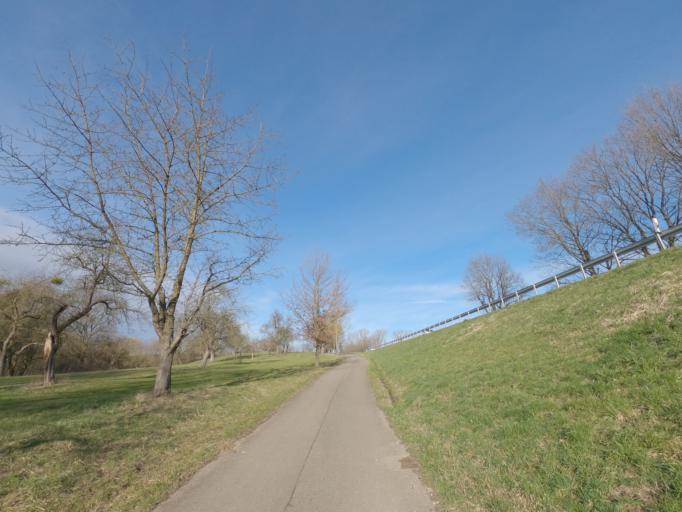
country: DE
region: Baden-Wuerttemberg
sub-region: Regierungsbezirk Stuttgart
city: Zell unter Aichelberg
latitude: 48.6417
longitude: 9.5875
